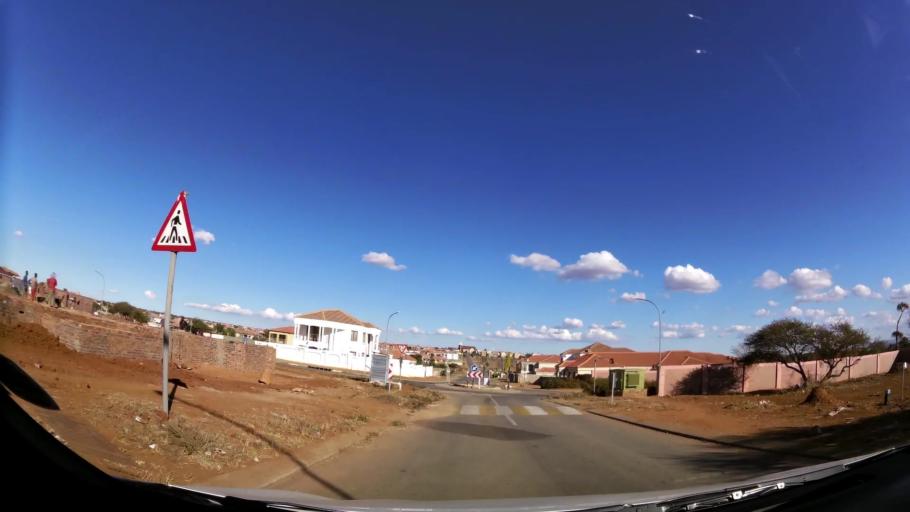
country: ZA
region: Limpopo
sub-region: Capricorn District Municipality
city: Polokwane
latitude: -23.9018
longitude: 29.5014
